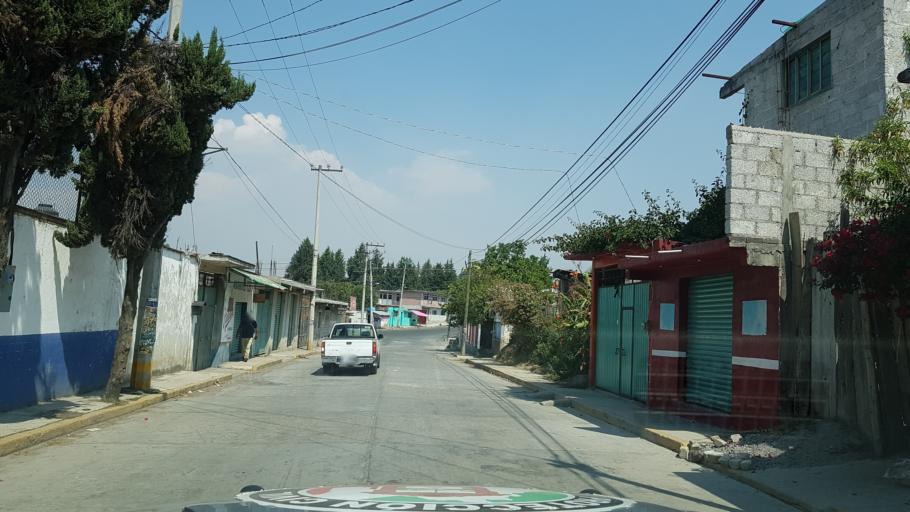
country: MX
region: Mexico
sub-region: Atlautla
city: San Juan Tepecoculco
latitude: 18.9868
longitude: -98.7903
